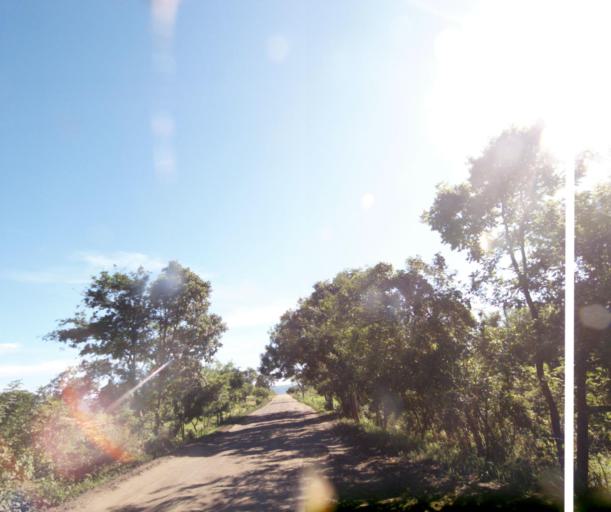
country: BR
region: Bahia
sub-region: Sao Felix Do Coribe
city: Santa Maria da Vitoria
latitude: -13.6281
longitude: -44.4237
